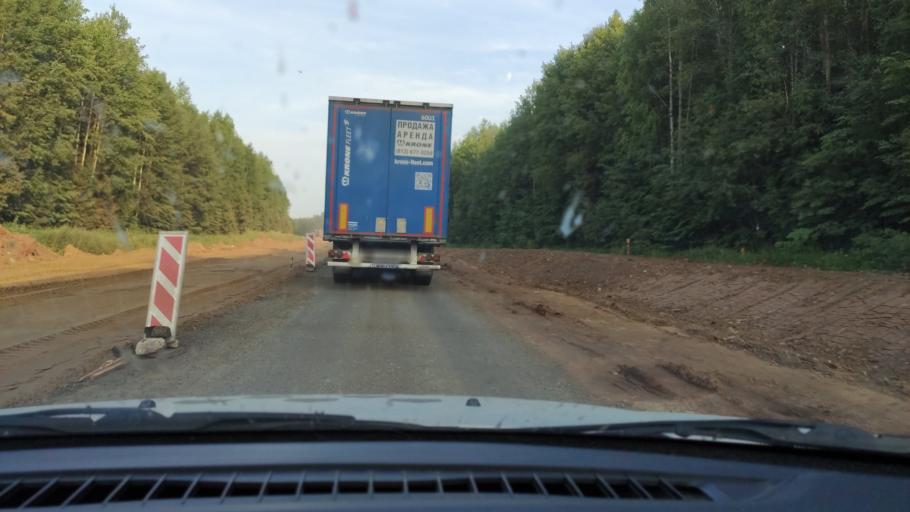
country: RU
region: Perm
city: Siva
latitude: 58.4868
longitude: 54.3673
